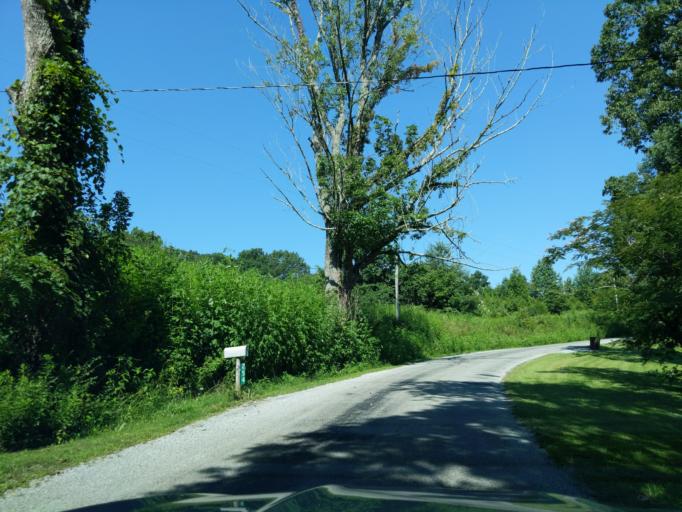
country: US
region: Indiana
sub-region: Ripley County
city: Osgood
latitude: 39.0766
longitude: -85.4277
